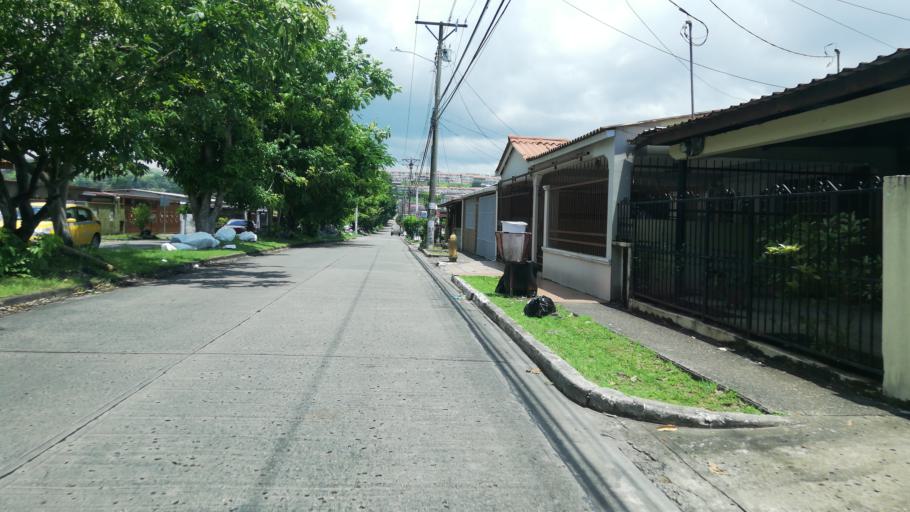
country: PA
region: Panama
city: San Miguelito
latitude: 9.0563
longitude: -79.4556
